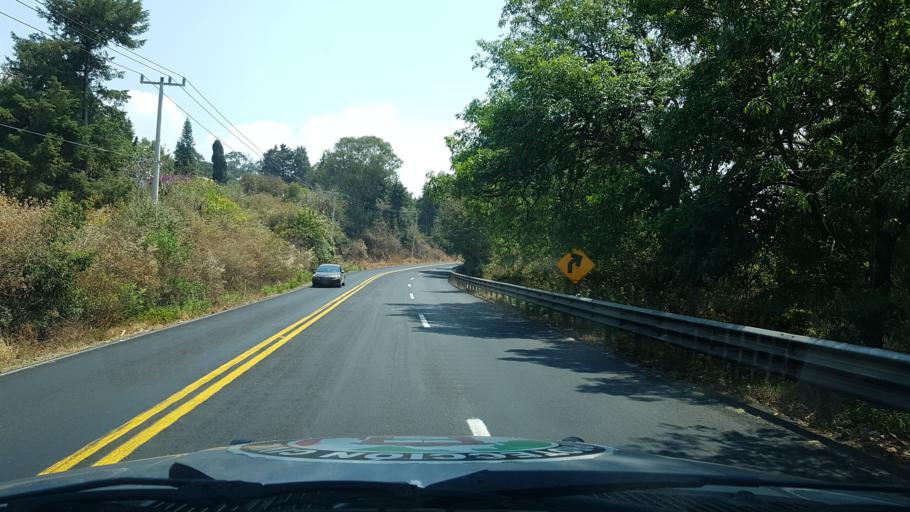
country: MX
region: Mexico
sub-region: Tepetlixpa
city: Nepantla de Sor Juana Ines de la Cruz
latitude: 18.9844
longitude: -98.8397
